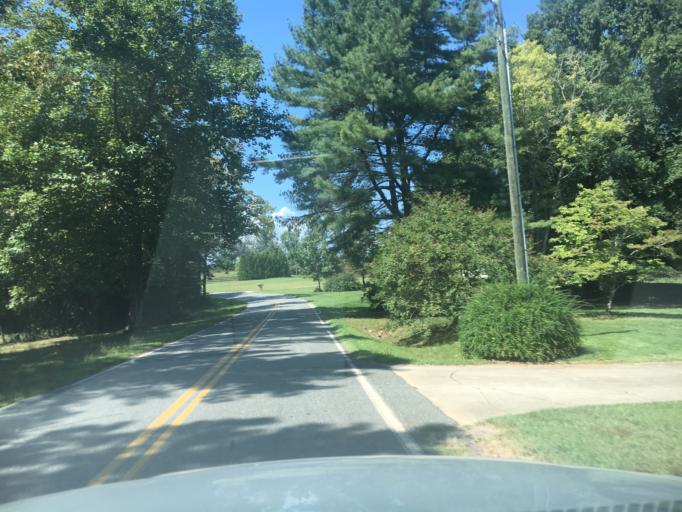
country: US
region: South Carolina
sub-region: Spartanburg County
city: Landrum
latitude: 35.1940
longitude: -82.0368
